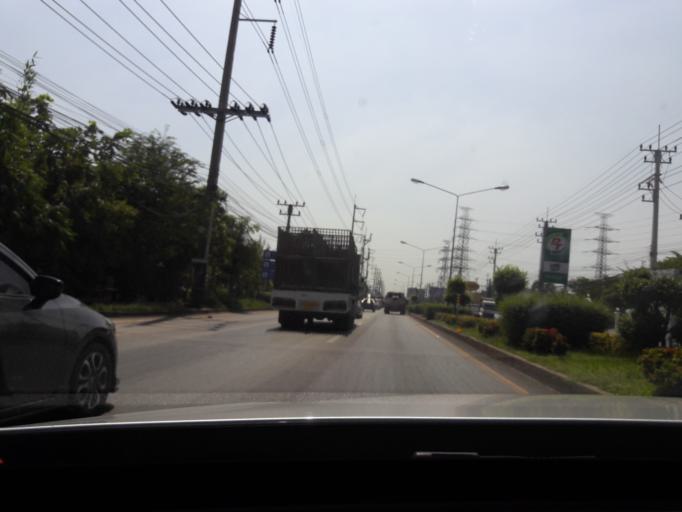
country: TH
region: Samut Sakhon
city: Samut Sakhon
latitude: 13.5964
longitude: 100.2826
